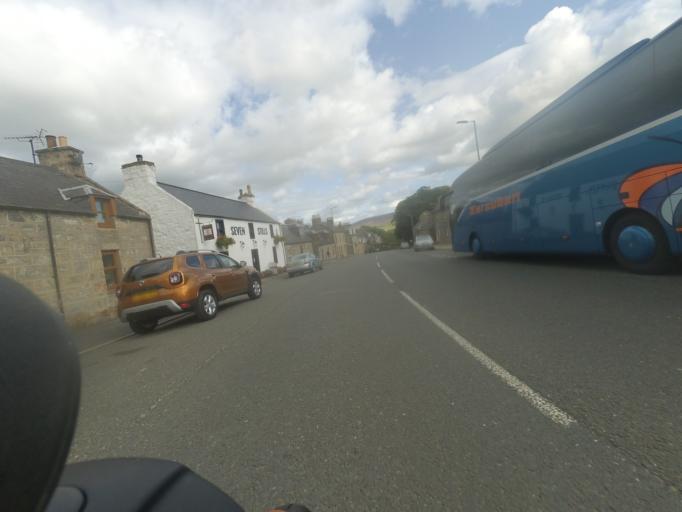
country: GB
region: Scotland
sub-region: Moray
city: Dufftown
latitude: 57.4449
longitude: -3.1262
